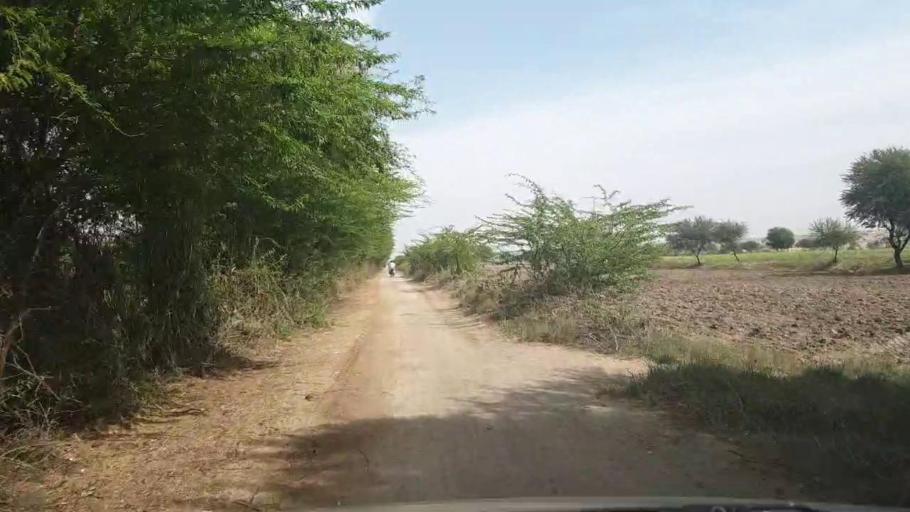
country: PK
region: Sindh
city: Kunri
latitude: 25.2036
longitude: 69.6936
